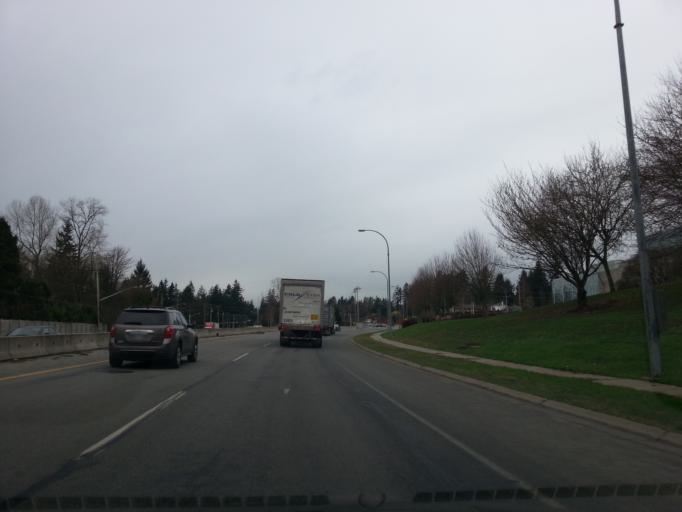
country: CA
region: British Columbia
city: Surrey
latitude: 49.1046
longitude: -122.8266
